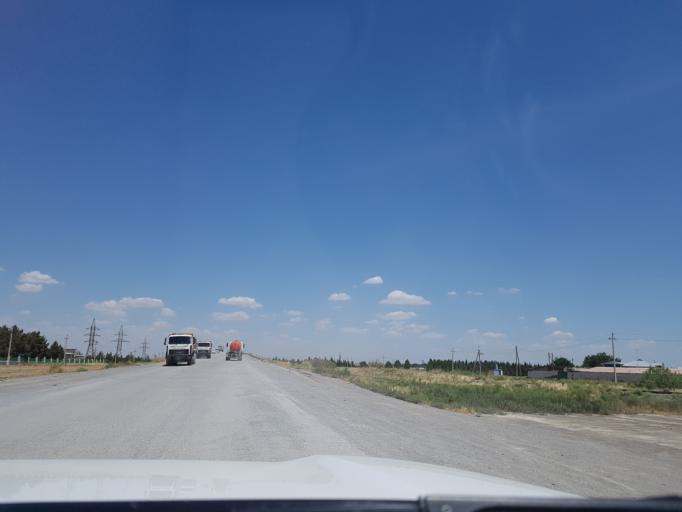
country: TM
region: Ahal
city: Abadan
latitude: 38.1702
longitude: 57.9365
